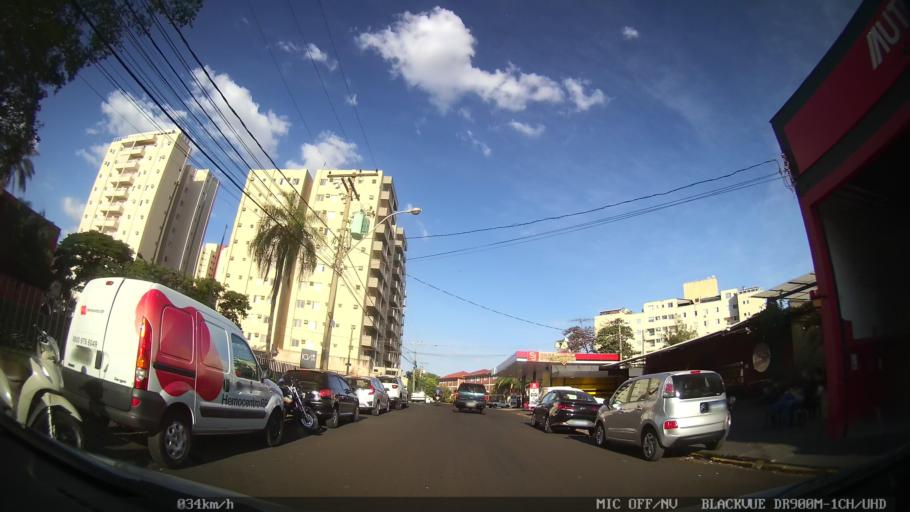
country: BR
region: Sao Paulo
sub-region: Ribeirao Preto
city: Ribeirao Preto
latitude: -21.1843
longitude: -47.7909
